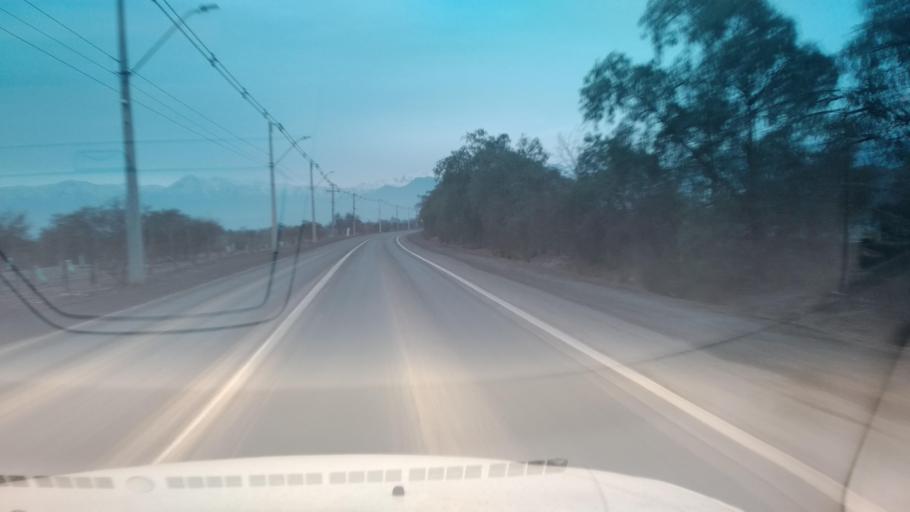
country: CL
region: Santiago Metropolitan
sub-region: Provincia de Chacabuco
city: Chicureo Abajo
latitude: -33.0956
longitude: -70.7493
